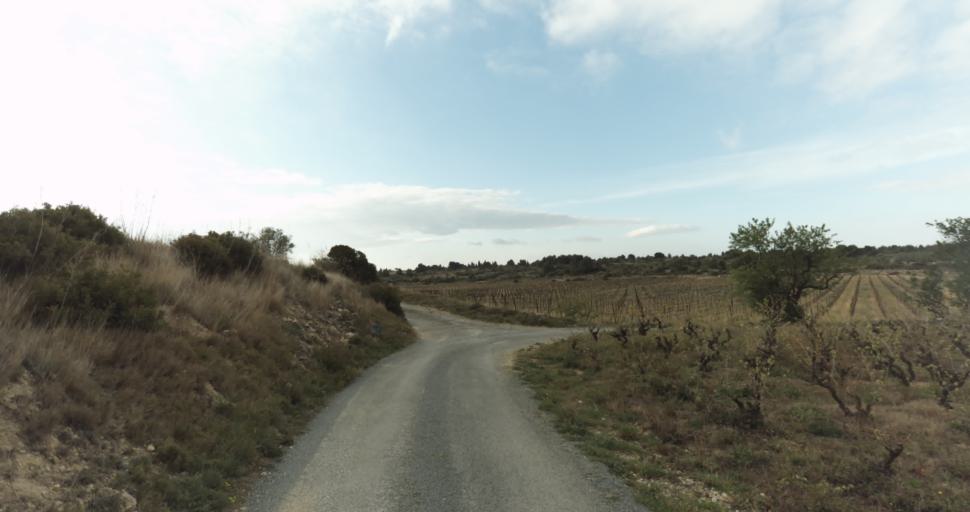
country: FR
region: Languedoc-Roussillon
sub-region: Departement de l'Aude
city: Leucate
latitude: 42.9292
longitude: 3.0256
